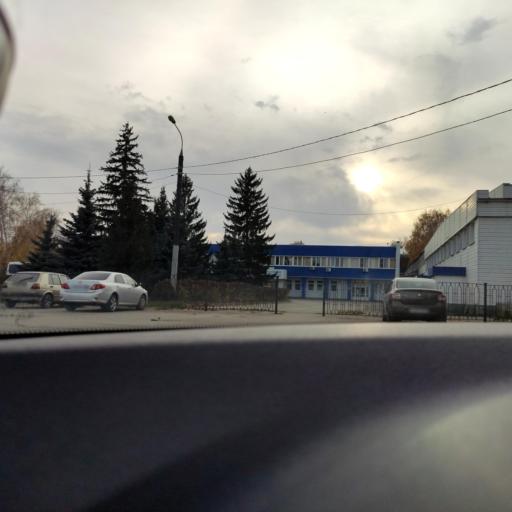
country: RU
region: Samara
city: Smyshlyayevka
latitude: 53.1894
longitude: 50.2762
